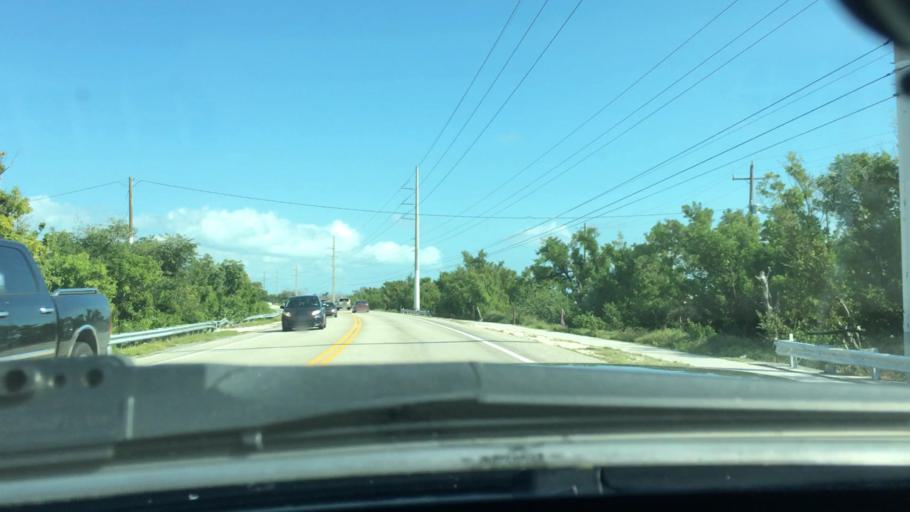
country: US
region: Florida
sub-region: Monroe County
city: Big Pine Key
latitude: 24.6501
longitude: -81.3098
